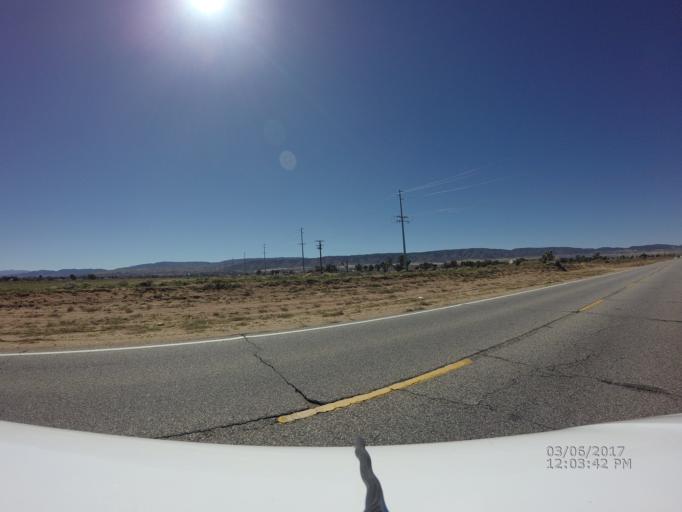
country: US
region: California
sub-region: Los Angeles County
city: Quartz Hill
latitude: 34.6749
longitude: -118.2273
